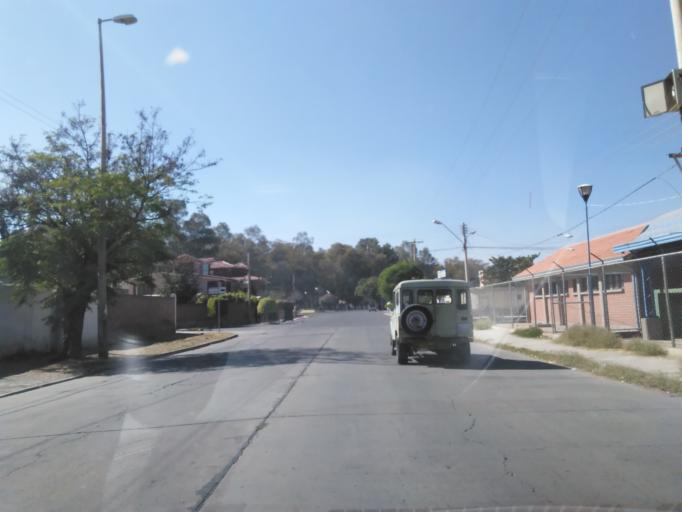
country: BO
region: Cochabamba
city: Cochabamba
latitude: -17.4005
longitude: -66.1774
